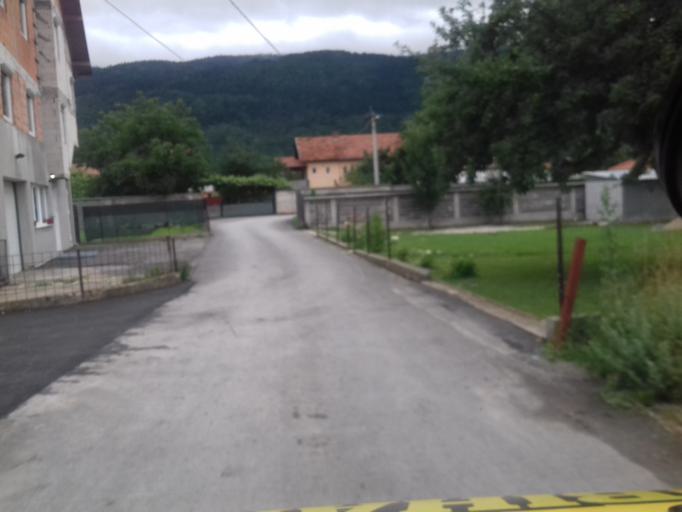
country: BA
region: Federation of Bosnia and Herzegovina
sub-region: Kanton Sarajevo
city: Sarajevo
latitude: 43.8131
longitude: 18.3063
